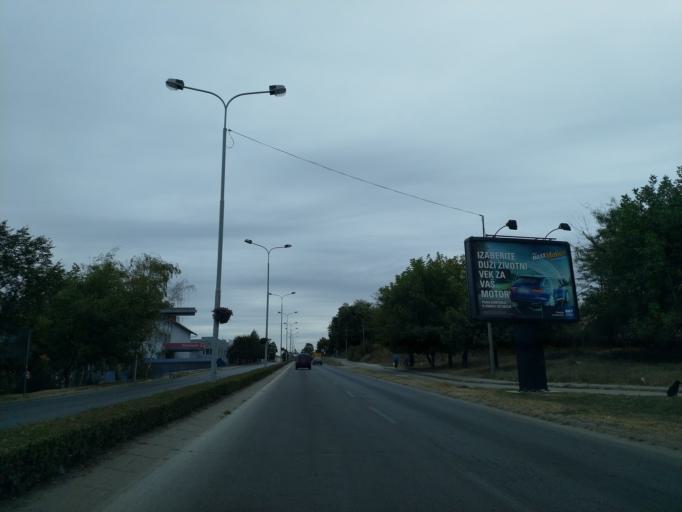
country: RS
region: Central Serbia
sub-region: Pomoravski Okrug
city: Jagodina
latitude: 43.9650
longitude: 21.2772
